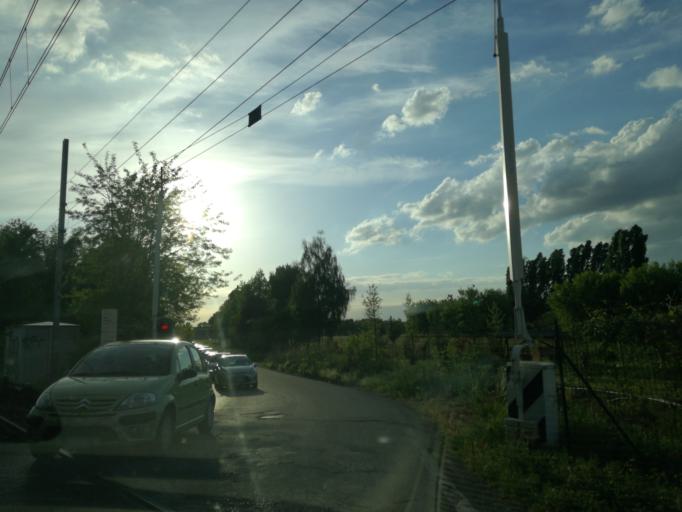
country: IT
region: Lombardy
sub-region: Provincia di Lecco
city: Merate
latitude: 45.6749
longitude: 9.4211
